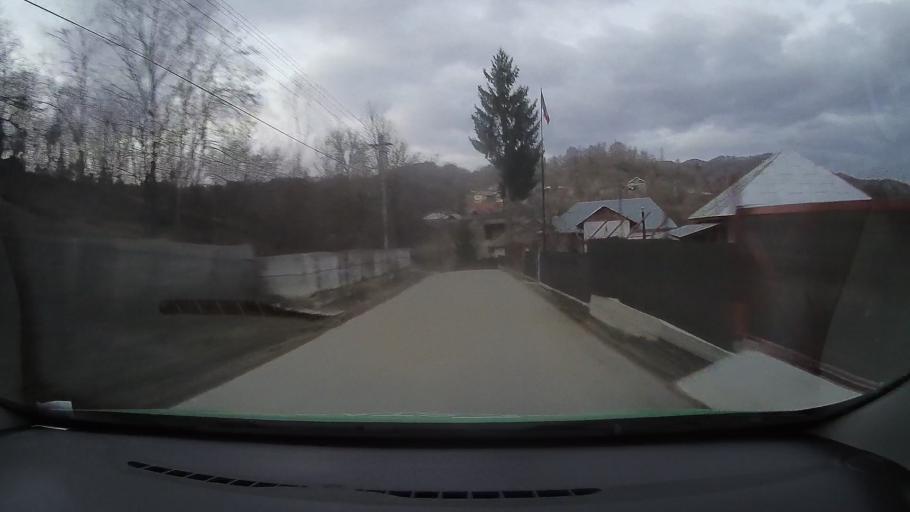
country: RO
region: Prahova
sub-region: Comuna Adunati
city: Adunati
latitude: 45.1117
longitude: 25.5859
